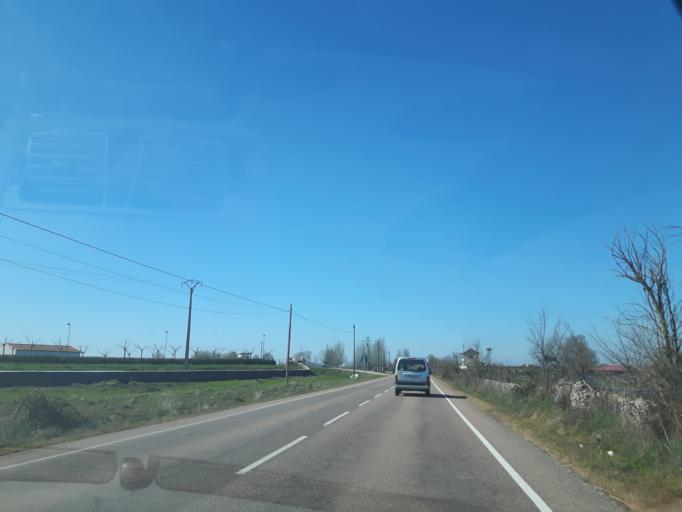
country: ES
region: Castille and Leon
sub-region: Provincia de Salamanca
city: Lumbrales
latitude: 40.9415
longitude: -6.6999
